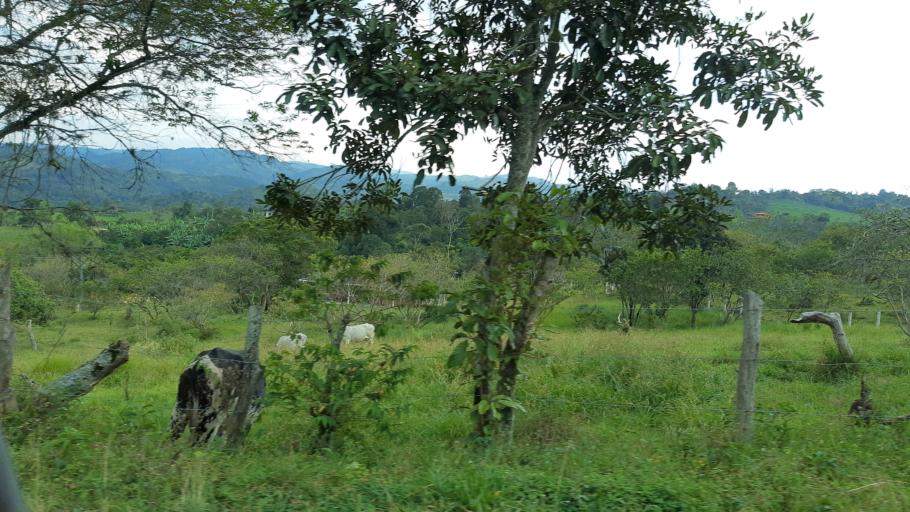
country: CO
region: Boyaca
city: Moniquira
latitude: 5.8353
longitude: -73.5913
